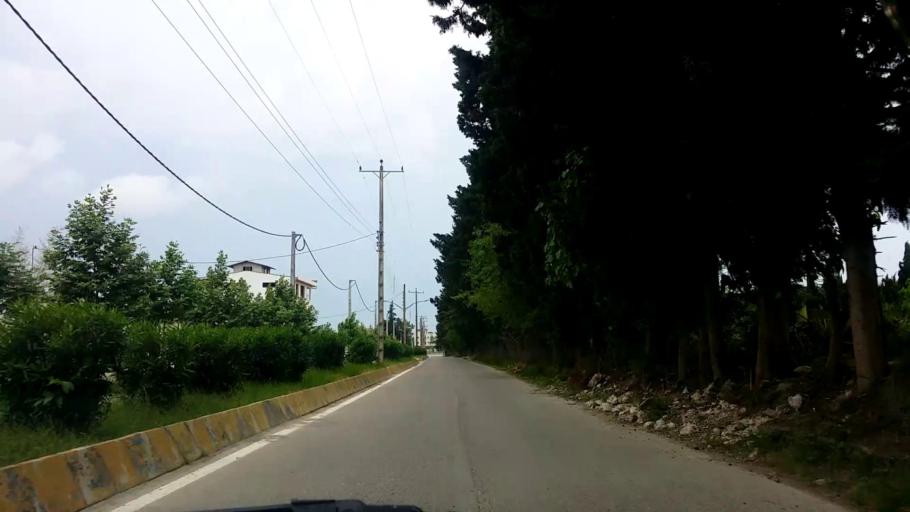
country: IR
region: Mazandaran
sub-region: Nowshahr
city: Nowshahr
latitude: 36.6344
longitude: 51.5026
